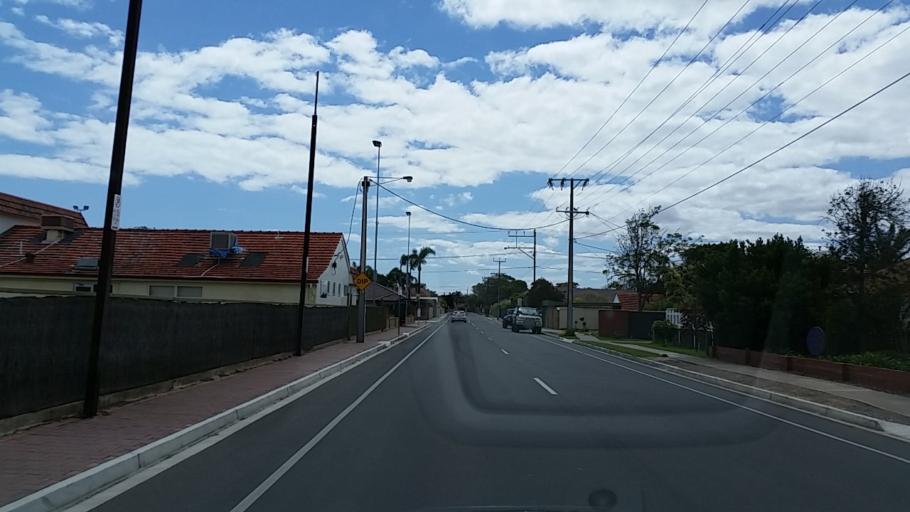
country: AU
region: South Australia
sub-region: Holdfast Bay
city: North Brighton
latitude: -35.0002
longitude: 138.5172
